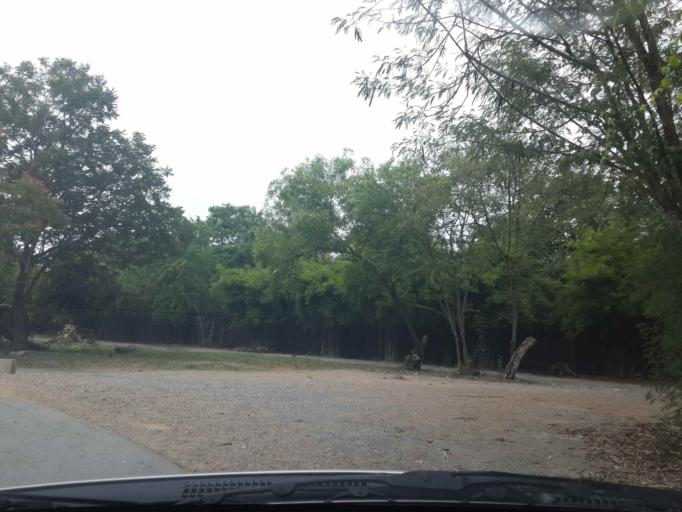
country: TH
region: Bangkok
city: Khan Na Yao
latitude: 13.8674
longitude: 100.7000
